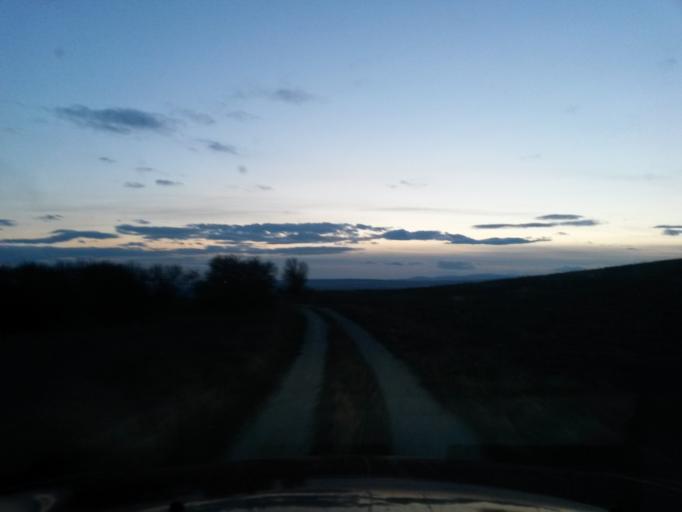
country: SK
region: Kosicky
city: Kosice
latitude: 48.6888
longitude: 21.3648
